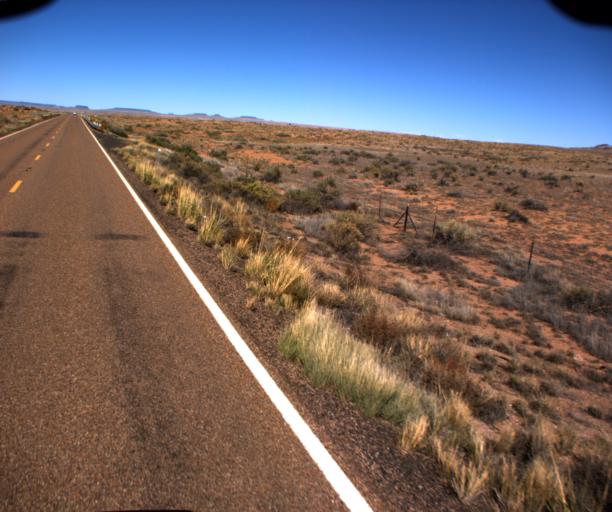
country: US
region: Arizona
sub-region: Navajo County
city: Holbrook
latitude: 35.0265
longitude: -110.0905
